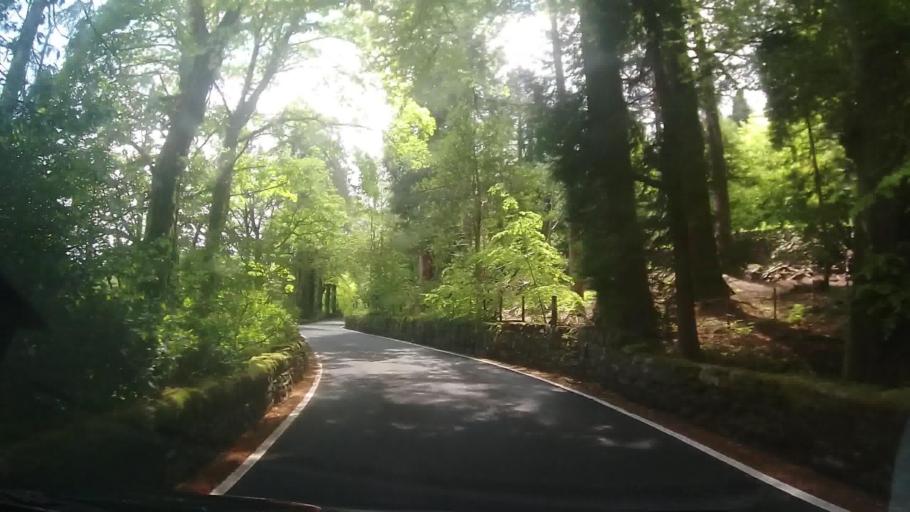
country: GB
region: Wales
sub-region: Gwynedd
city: Penrhyndeudraeth
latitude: 52.9931
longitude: -4.0959
